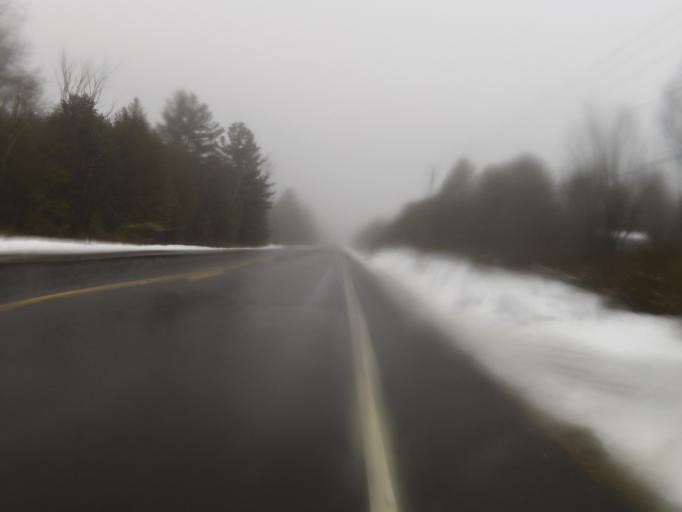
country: CA
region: Ontario
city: Perth
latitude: 44.8095
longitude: -76.4015
